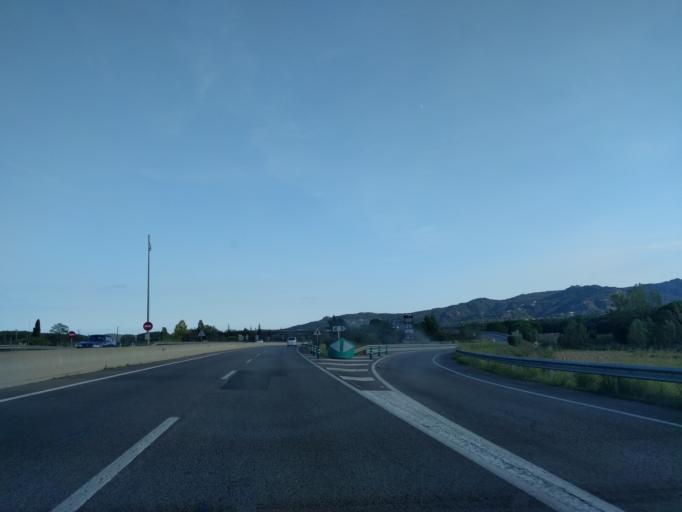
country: ES
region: Catalonia
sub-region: Provincia de Girona
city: Santa Cristina d'Aro
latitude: 41.8245
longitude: 2.9745
